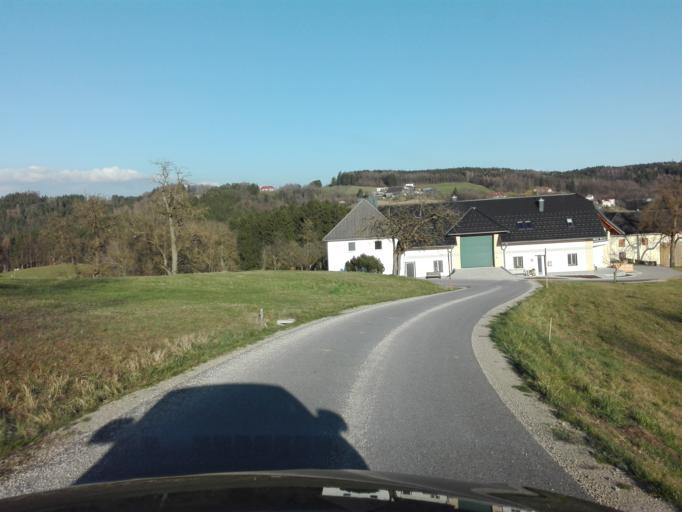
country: AT
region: Upper Austria
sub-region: Politischer Bezirk Perg
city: Bad Kreuzen
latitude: 48.2365
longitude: 14.7376
